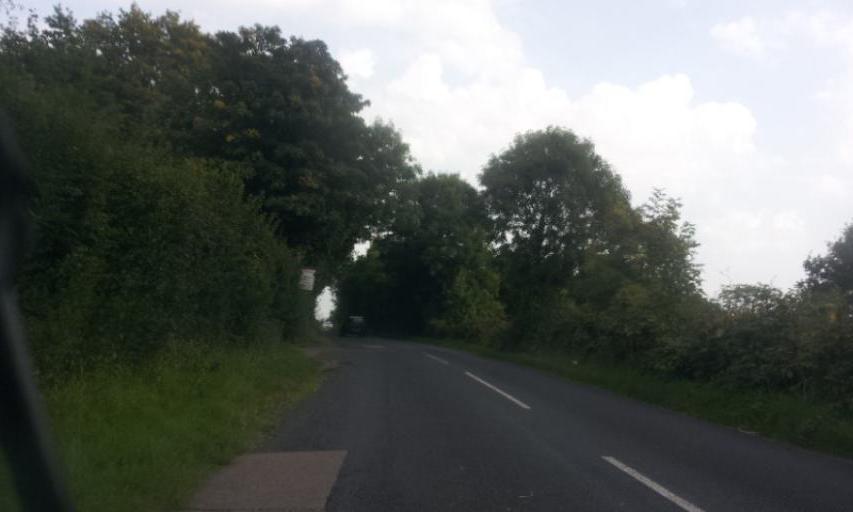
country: GB
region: England
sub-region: Kent
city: Paddock Wood
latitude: 51.1554
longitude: 0.3699
